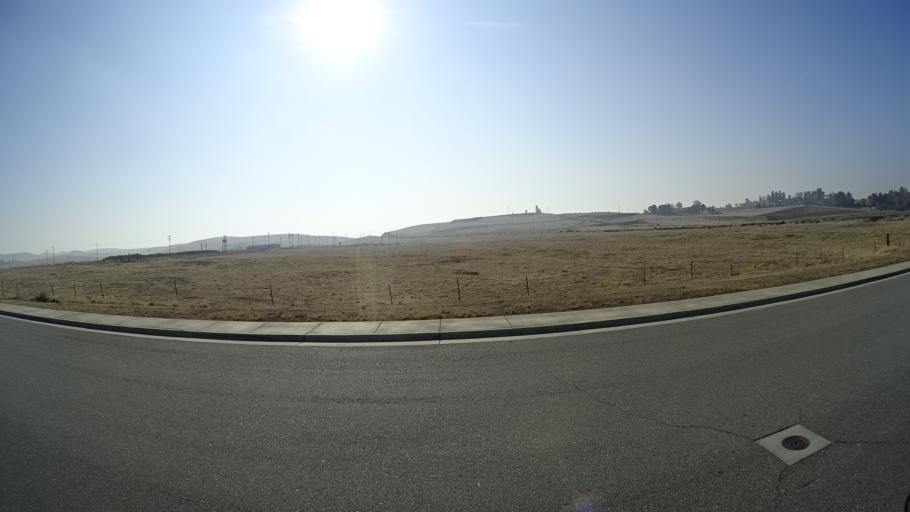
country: US
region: California
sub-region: Kern County
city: Lamont
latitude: 35.4057
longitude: -118.8577
